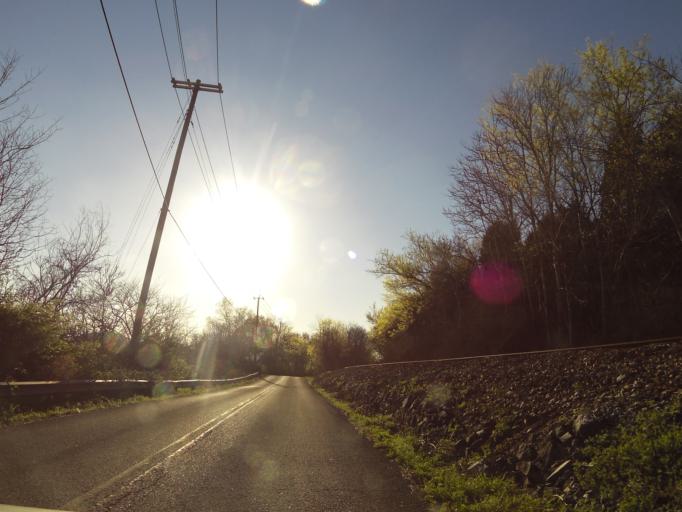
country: US
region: Tennessee
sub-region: Knox County
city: Knoxville
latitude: 35.9596
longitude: -83.8448
